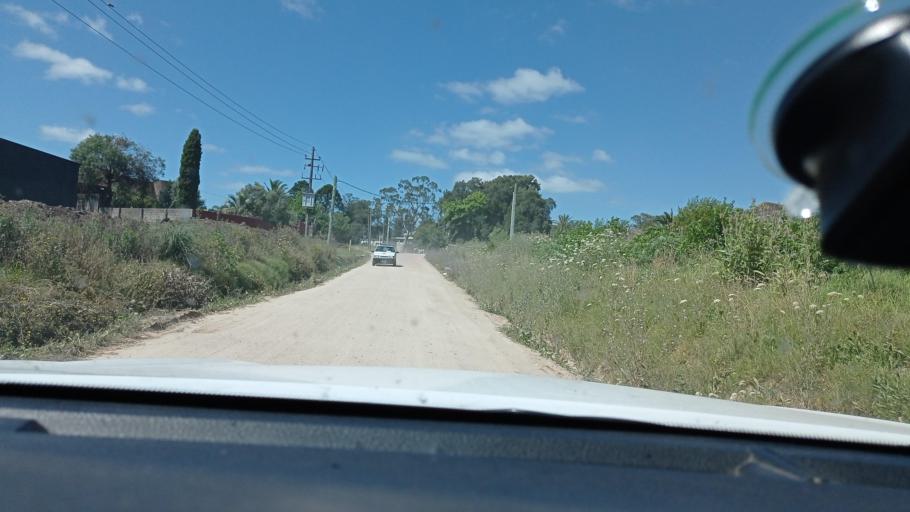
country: UY
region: Canelones
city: Pando
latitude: -34.7316
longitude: -55.9756
